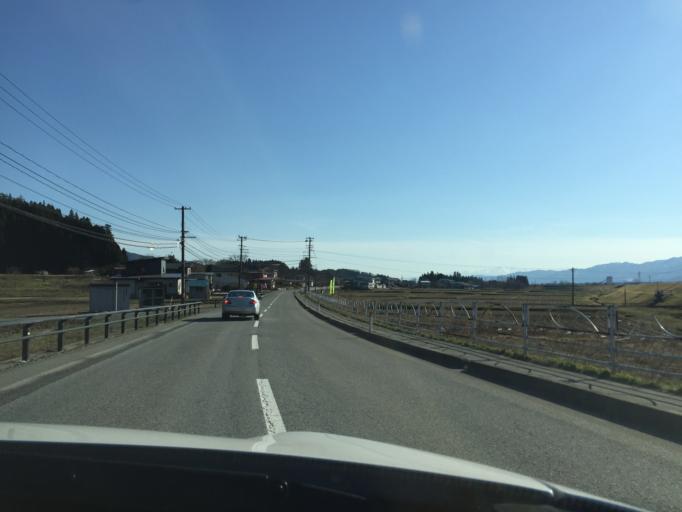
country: JP
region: Yamagata
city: Nagai
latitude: 38.1985
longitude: 140.1036
